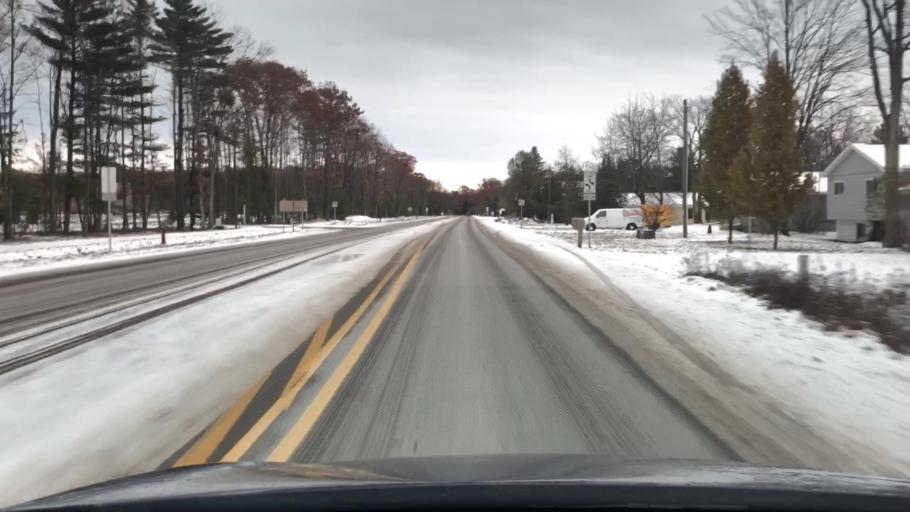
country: US
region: Michigan
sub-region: Grand Traverse County
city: Traverse City
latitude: 44.7332
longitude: -85.5739
